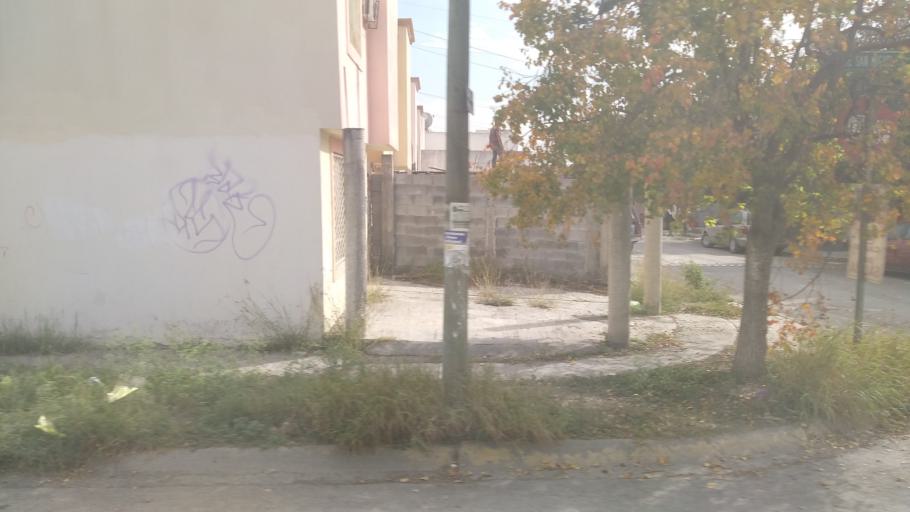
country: MX
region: Nuevo Leon
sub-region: Apodaca
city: Loma la Paz
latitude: 25.7038
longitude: -100.1425
